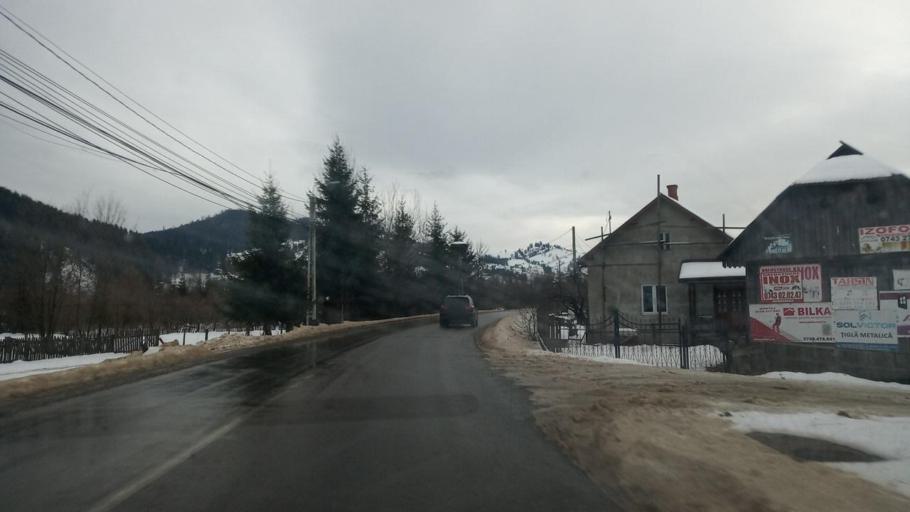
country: RO
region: Suceava
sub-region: Comuna Frasin
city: Frasin
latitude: 47.5168
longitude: 25.8002
